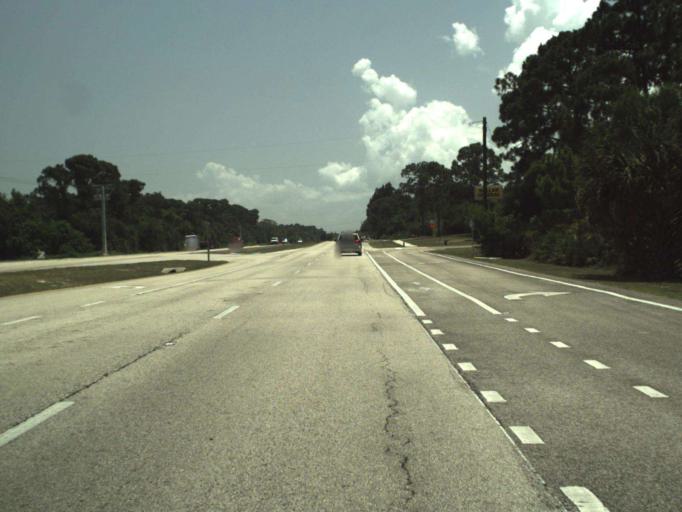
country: US
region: Florida
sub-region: Volusia County
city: Edgewater
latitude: 28.9532
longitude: -80.8857
